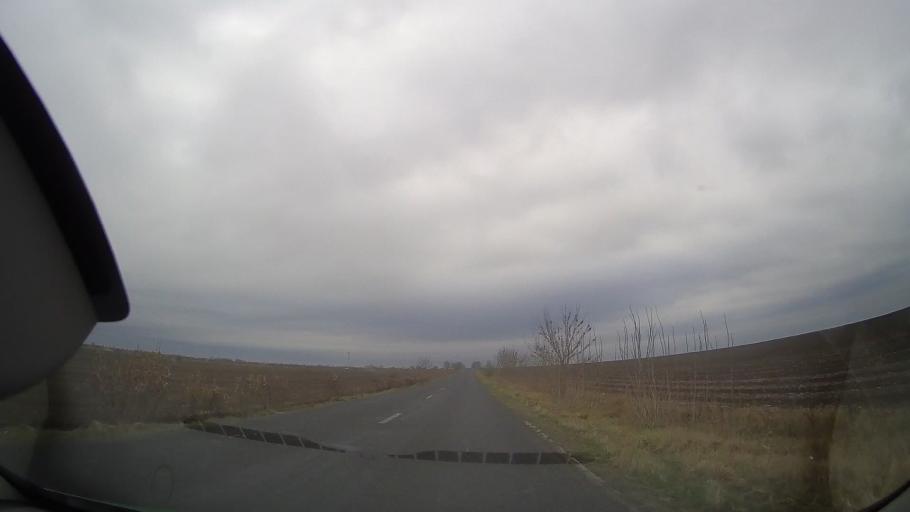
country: RO
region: Buzau
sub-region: Comuna Padina
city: Padina
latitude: 44.7874
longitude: 27.1465
